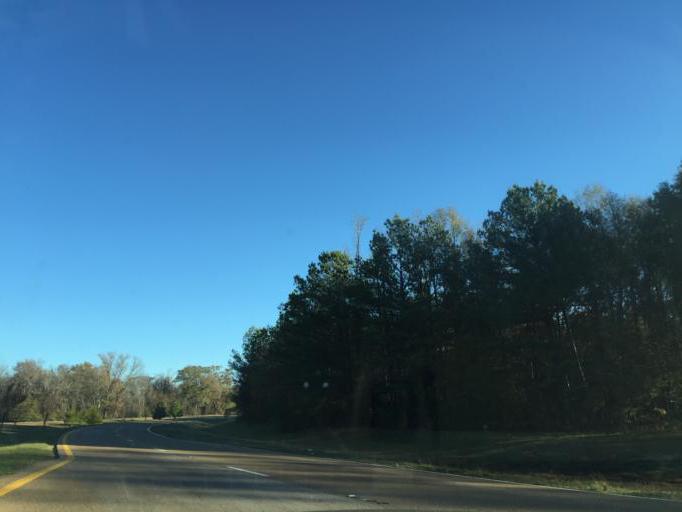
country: US
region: Mississippi
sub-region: Rankin County
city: Pearl
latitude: 32.2857
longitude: -90.1566
